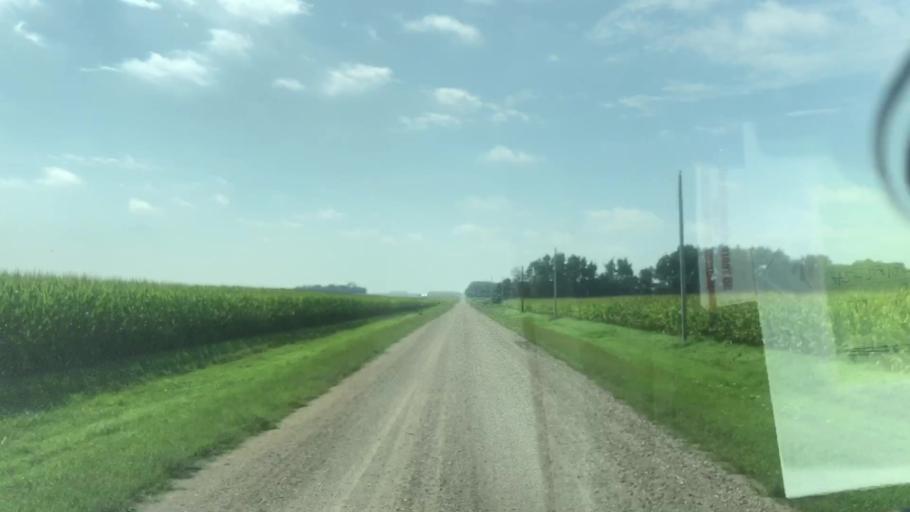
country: US
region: Iowa
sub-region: O'Brien County
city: Sheldon
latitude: 43.2001
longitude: -95.9417
